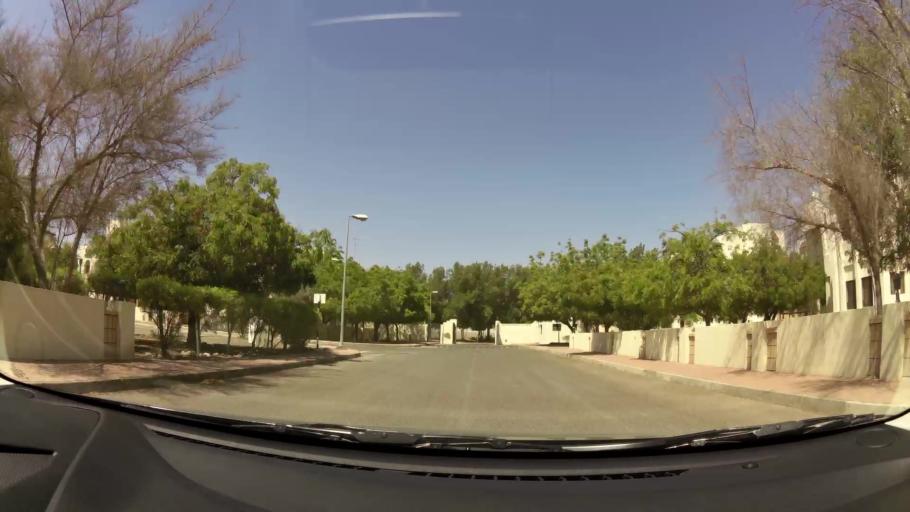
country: OM
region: Muhafazat Masqat
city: As Sib al Jadidah
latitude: 23.6157
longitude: 58.2453
